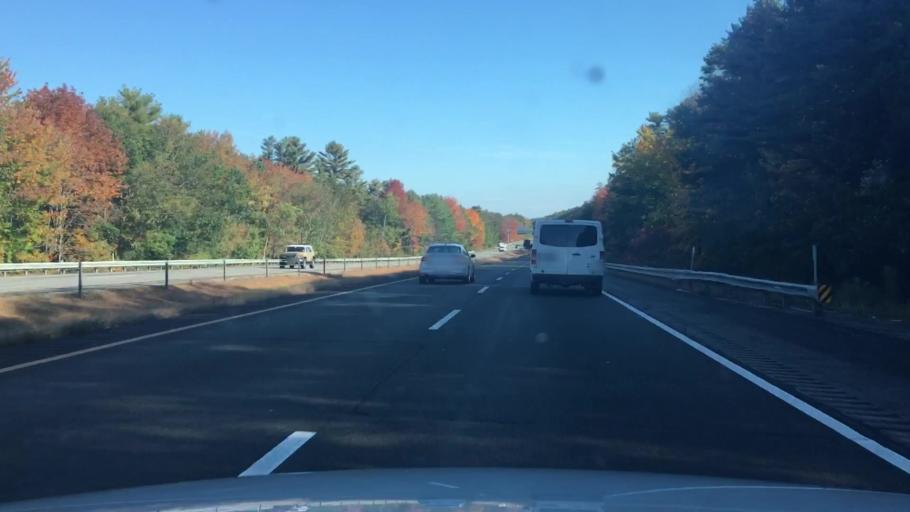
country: US
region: Maine
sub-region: Cumberland County
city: Falmouth Foreside
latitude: 43.7489
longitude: -70.2187
